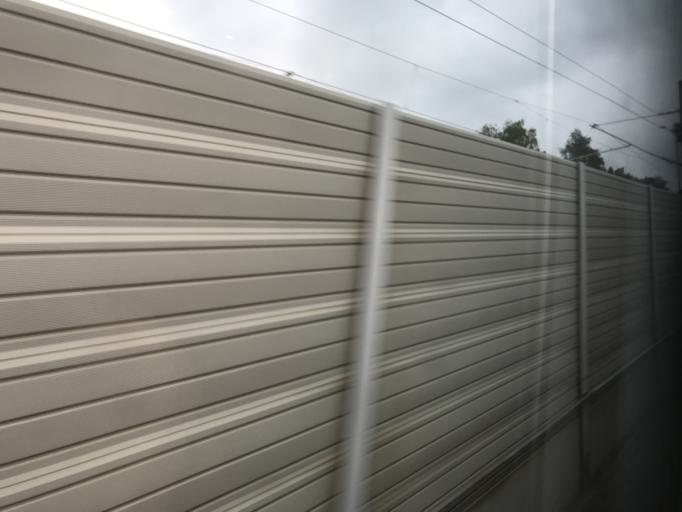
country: DE
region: Bavaria
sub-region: Upper Bavaria
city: Maisach
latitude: 48.2131
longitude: 11.2940
